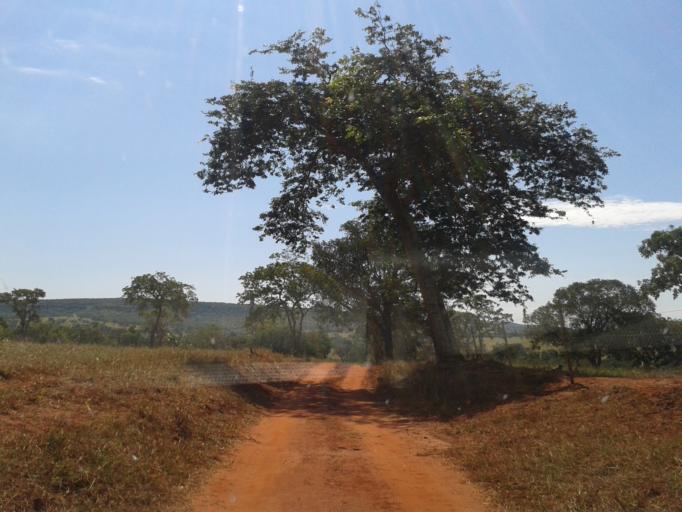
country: BR
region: Minas Gerais
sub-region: Campina Verde
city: Campina Verde
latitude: -19.3984
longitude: -49.7659
